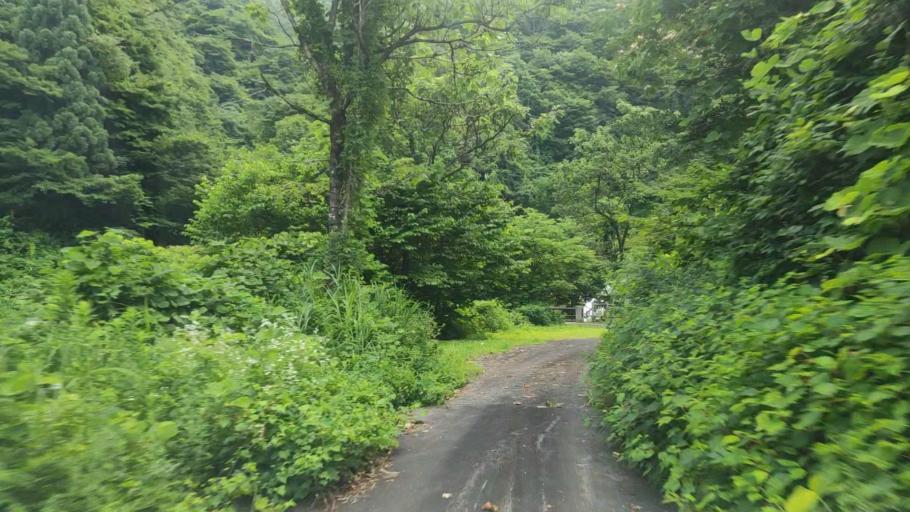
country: JP
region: Fukui
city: Ono
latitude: 35.8930
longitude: 136.5282
